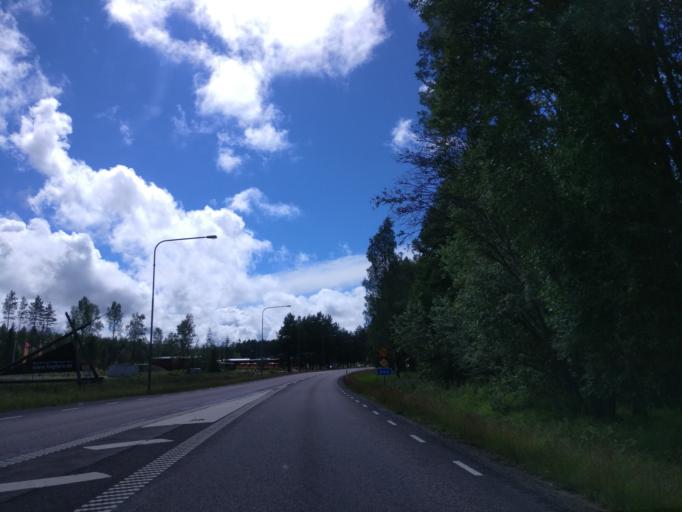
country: SE
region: Vaermland
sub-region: Hagfors Kommun
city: Hagfors
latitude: 60.0138
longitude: 13.6780
